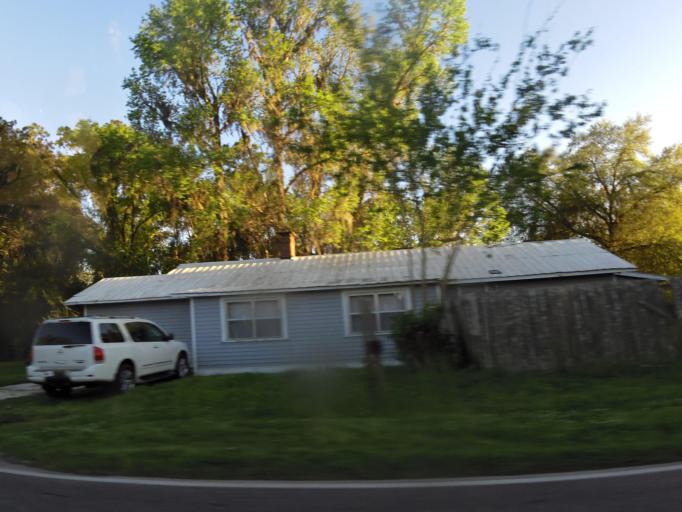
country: US
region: Florida
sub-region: Alachua County
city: Waldo
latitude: 29.8644
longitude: -82.1411
